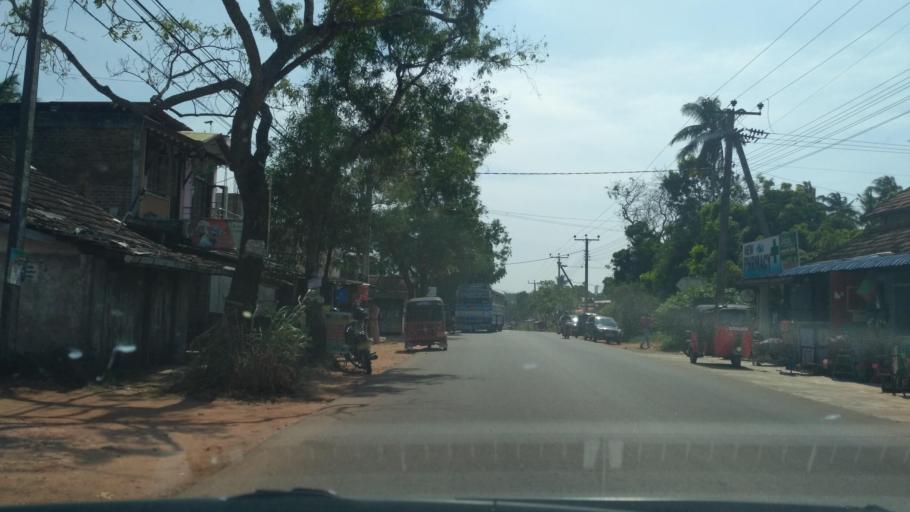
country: LK
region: North Western
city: Kuliyapitiya
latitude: 7.3613
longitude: 80.0337
